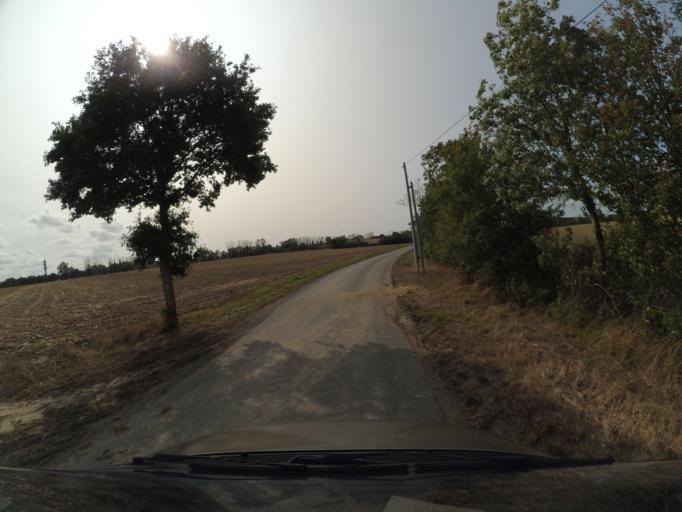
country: FR
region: Pays de la Loire
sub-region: Departement de la Vendee
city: Treize-Septiers
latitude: 46.9751
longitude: -1.2205
